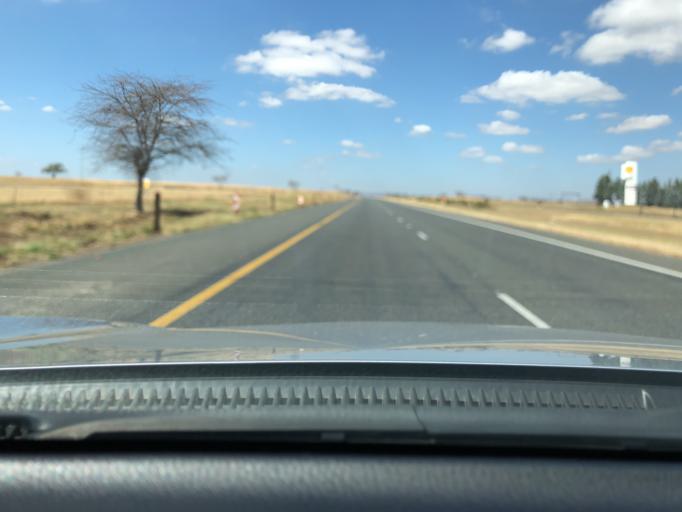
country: ZA
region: KwaZulu-Natal
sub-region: uThukela District Municipality
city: Estcourt
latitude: -28.9237
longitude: 29.7808
